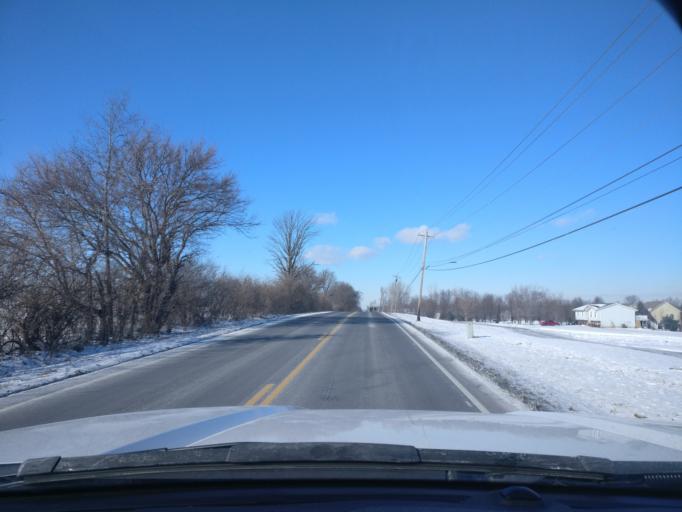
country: US
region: Ohio
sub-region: Warren County
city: Hunter
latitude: 39.5136
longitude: -84.2696
